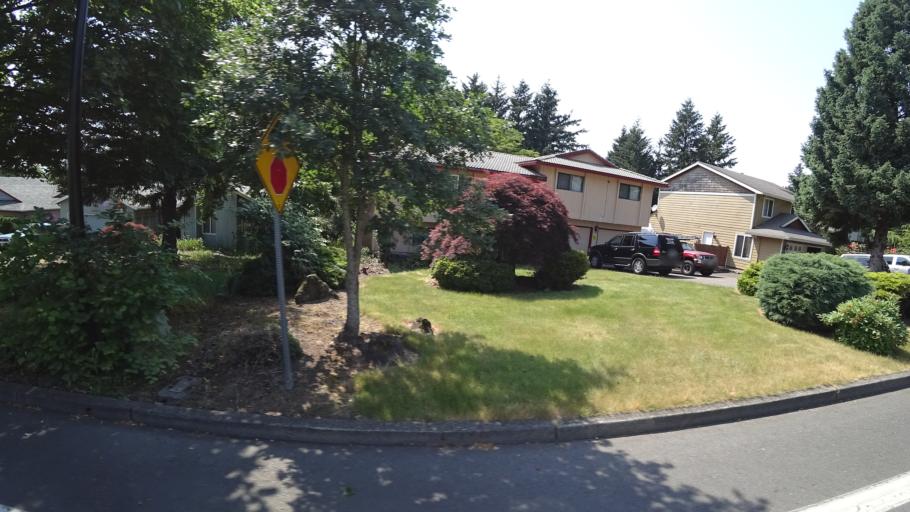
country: US
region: Oregon
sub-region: Clackamas County
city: Happy Valley
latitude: 45.4441
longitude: -122.5638
